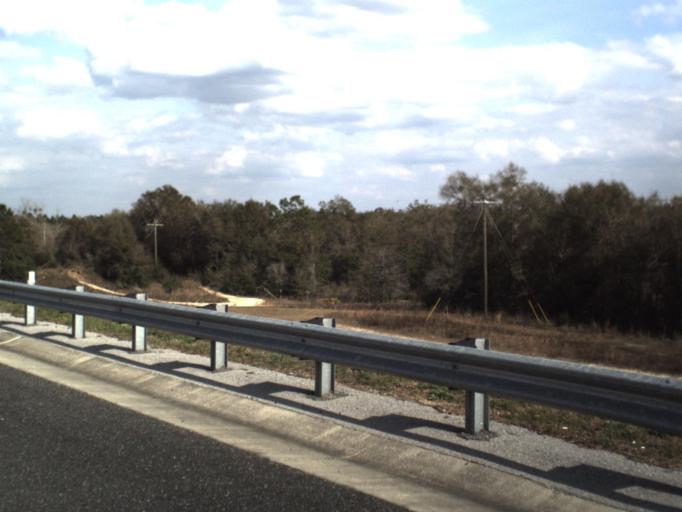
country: US
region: Florida
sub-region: Bay County
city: Youngstown
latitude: 30.5278
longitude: -85.4015
